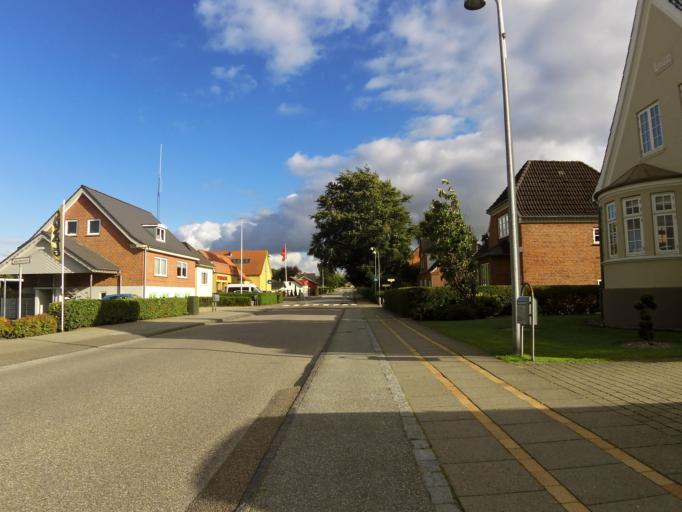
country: DK
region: South Denmark
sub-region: Tonder Kommune
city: Toftlund
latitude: 55.1890
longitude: 9.0650
